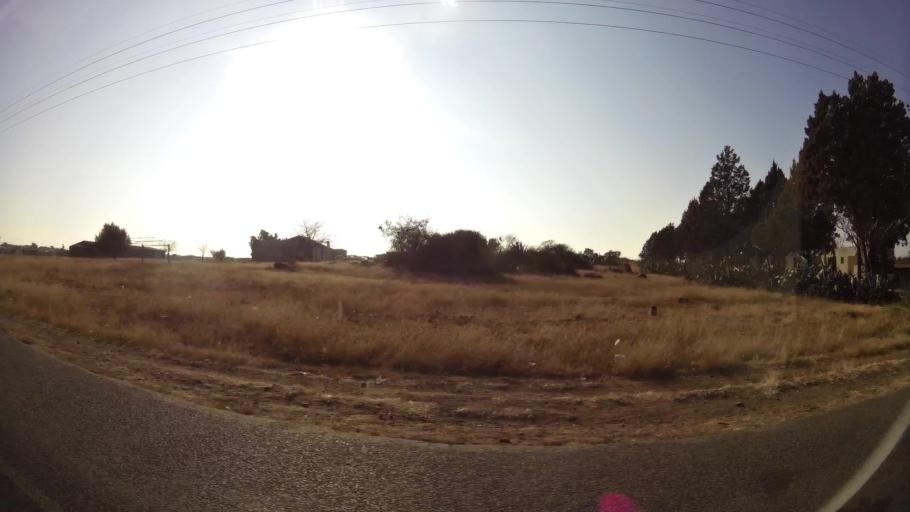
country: ZA
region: Orange Free State
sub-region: Mangaung Metropolitan Municipality
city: Bloemfontein
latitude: -29.1884
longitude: 26.2708
